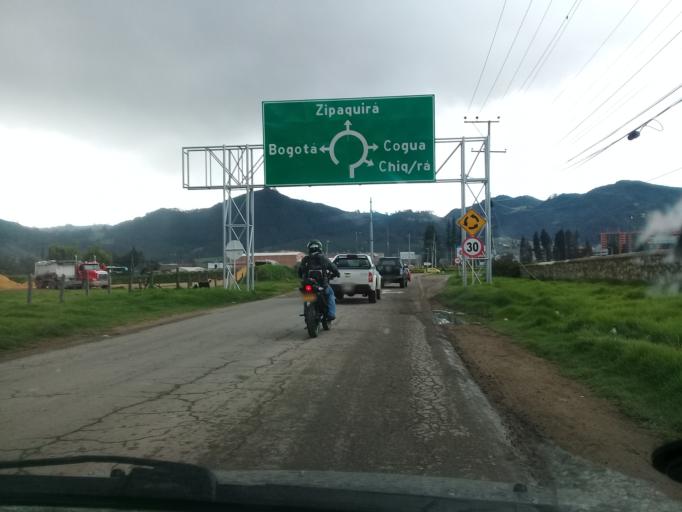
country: CO
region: Cundinamarca
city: Zipaquira
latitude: 5.0085
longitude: -73.9861
